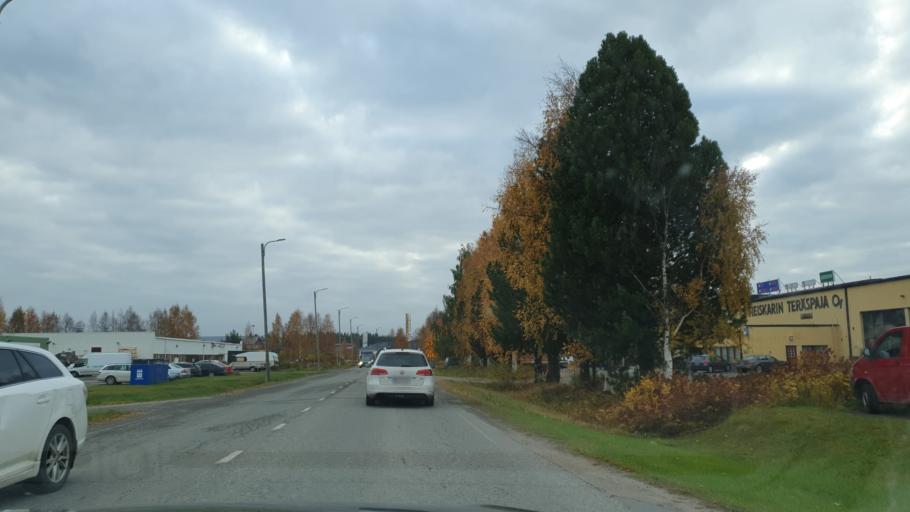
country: FI
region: Lapland
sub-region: Rovaniemi
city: Rovaniemi
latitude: 66.4925
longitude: 25.6683
